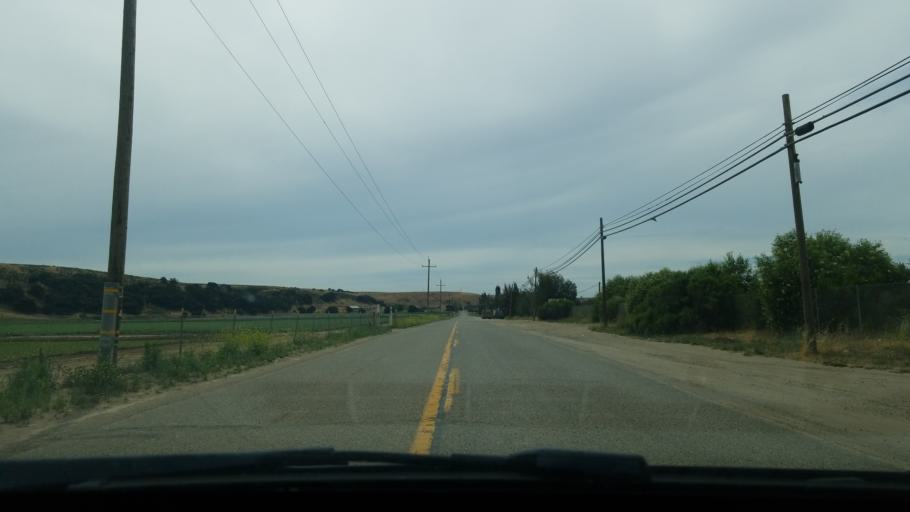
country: US
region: California
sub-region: Santa Barbara County
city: Los Alamos
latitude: 34.8645
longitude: -120.2795
